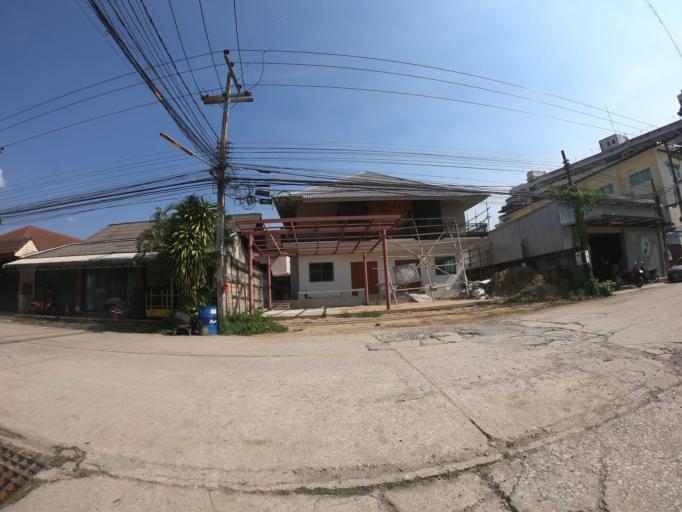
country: TH
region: Chiang Mai
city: Chiang Mai
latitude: 18.8088
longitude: 99.0007
